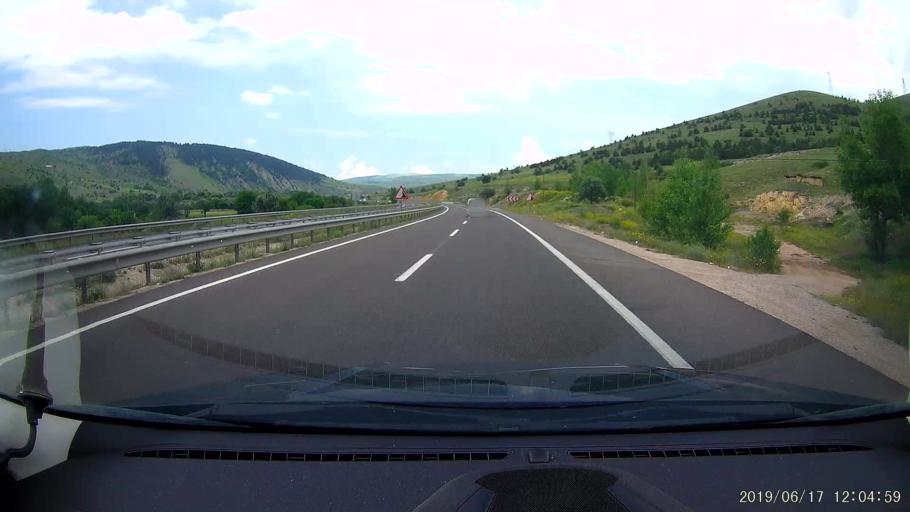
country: TR
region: Cankiri
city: Cerkes
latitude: 40.8278
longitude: 32.7884
